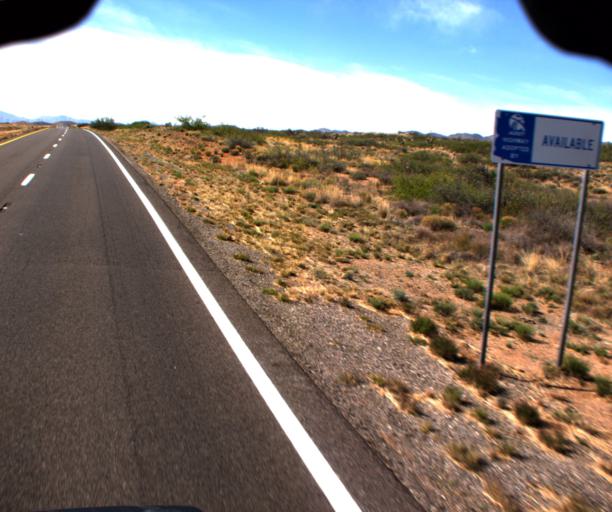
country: US
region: Arizona
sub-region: Graham County
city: Swift Trail Junction
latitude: 32.5061
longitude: -109.6743
